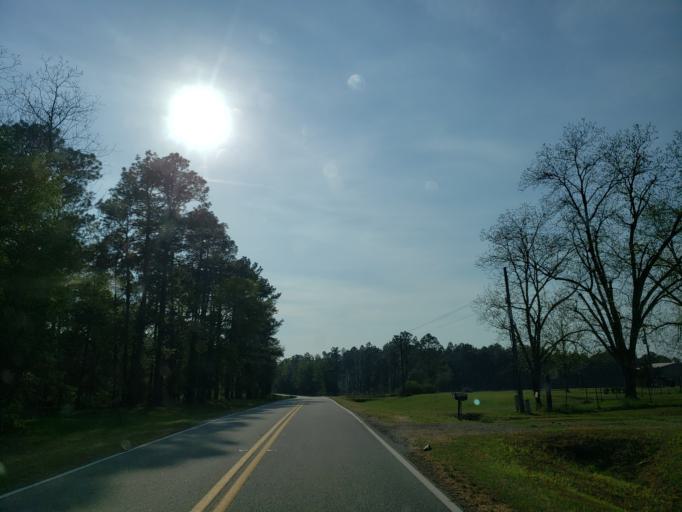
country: US
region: Georgia
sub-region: Tift County
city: Tifton
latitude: 31.5586
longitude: -83.5006
